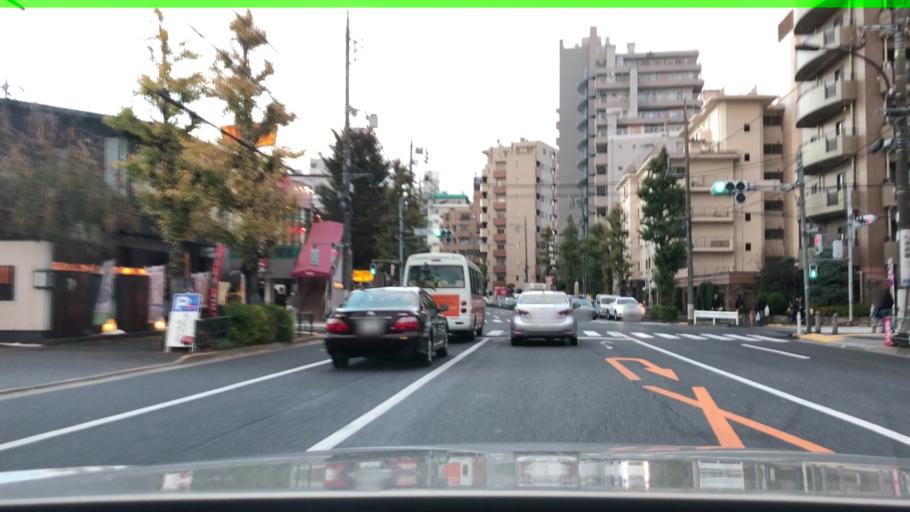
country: JP
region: Tokyo
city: Tokyo
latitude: 35.6139
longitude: 139.6660
